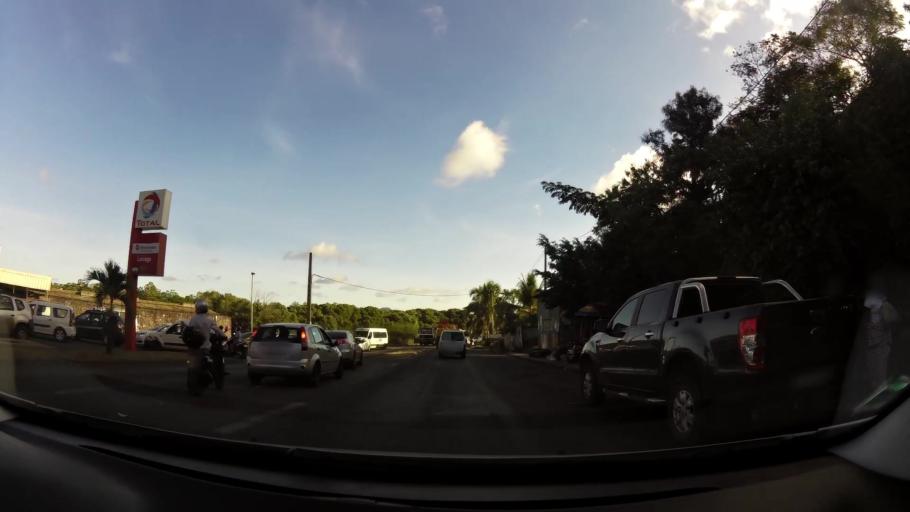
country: YT
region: Mamoudzou
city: Mamoudzou
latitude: -12.8062
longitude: 45.2085
